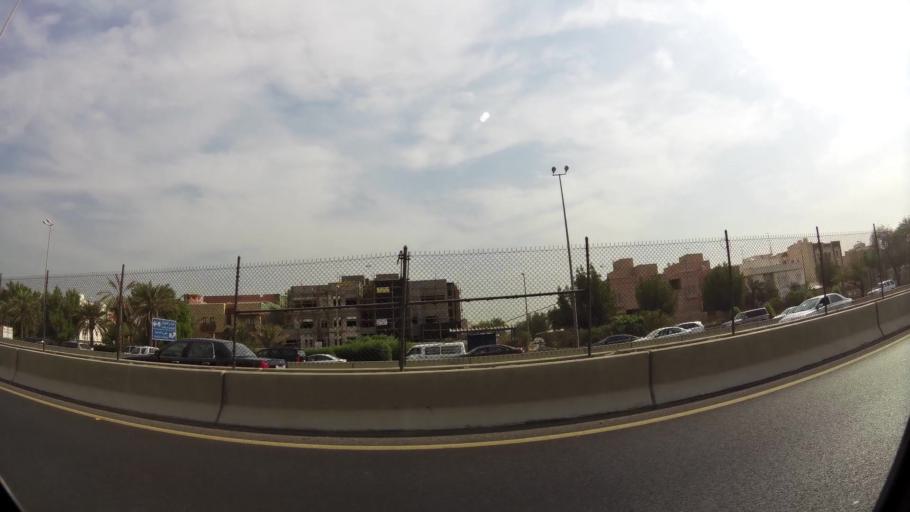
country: KW
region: Al Asimah
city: Ash Shamiyah
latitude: 29.3294
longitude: 47.9720
